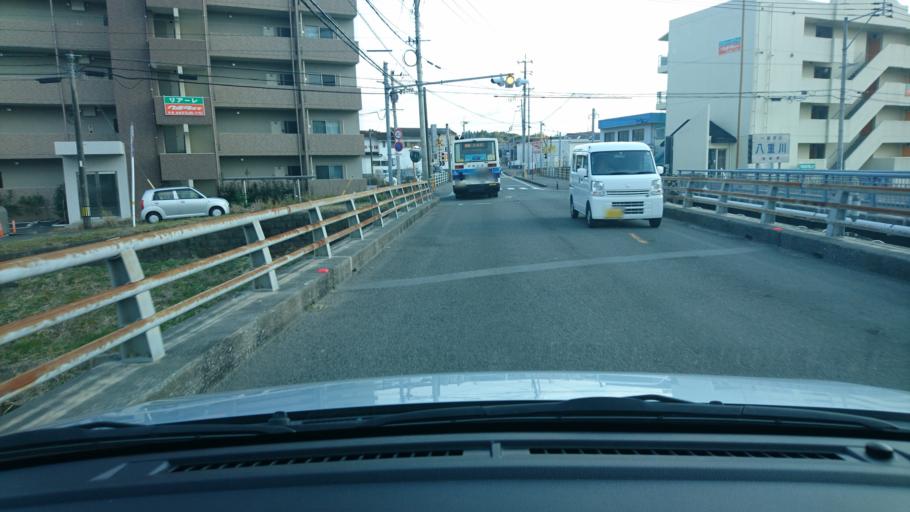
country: JP
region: Miyazaki
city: Miyazaki-shi
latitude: 31.8761
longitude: 131.4050
